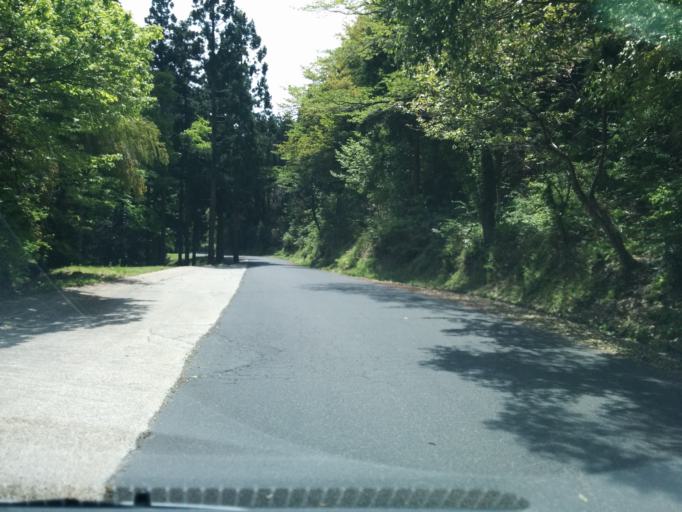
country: JP
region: Kyoto
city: Miyazu
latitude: 35.5950
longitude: 135.1847
